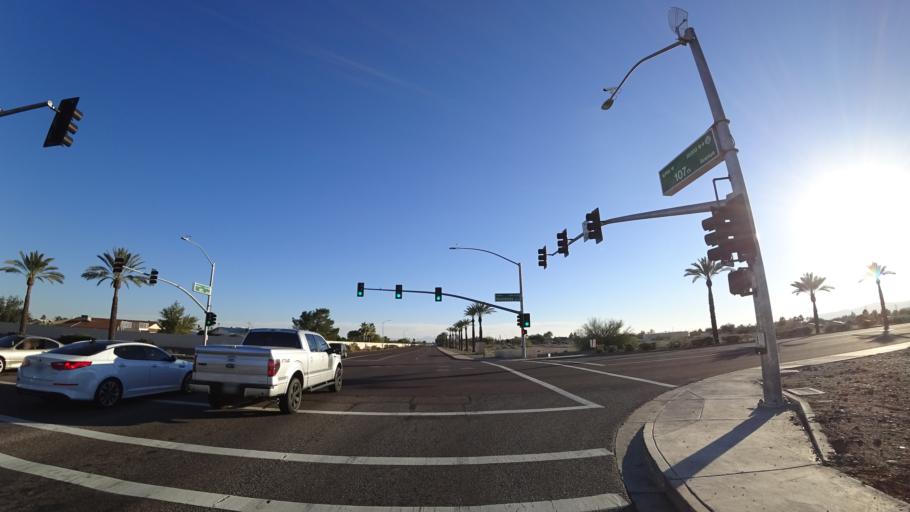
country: US
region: Arizona
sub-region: Maricopa County
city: Sun City West
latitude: 33.6674
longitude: -112.2901
